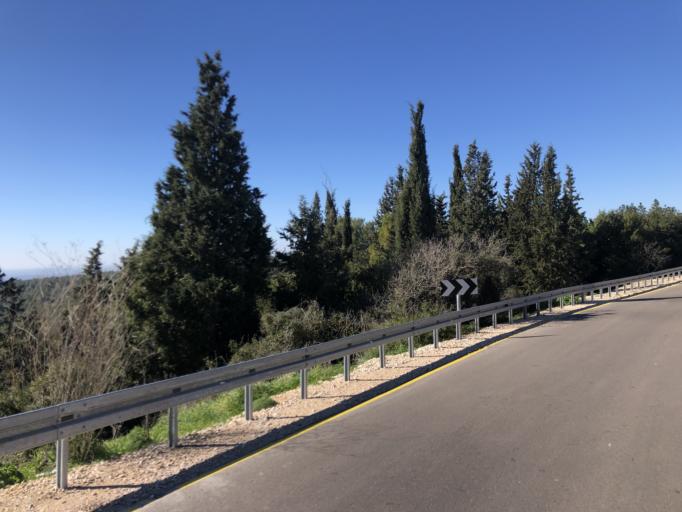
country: IL
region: Jerusalem
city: Zur Hadassa
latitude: 31.7462
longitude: 35.0498
